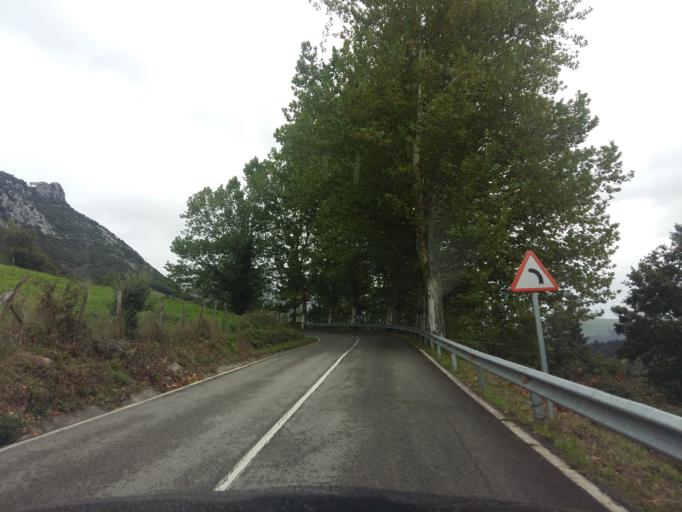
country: ES
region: Basque Country
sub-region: Bizkaia
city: Lanestosa
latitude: 43.1894
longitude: -3.5153
